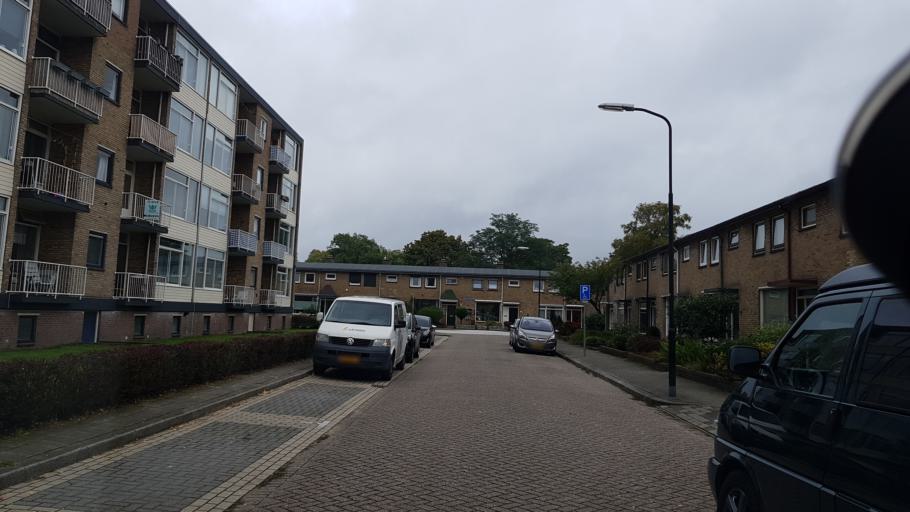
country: NL
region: Gelderland
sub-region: Gemeente Apeldoorn
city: Apeldoorn
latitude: 52.1920
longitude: 5.9580
